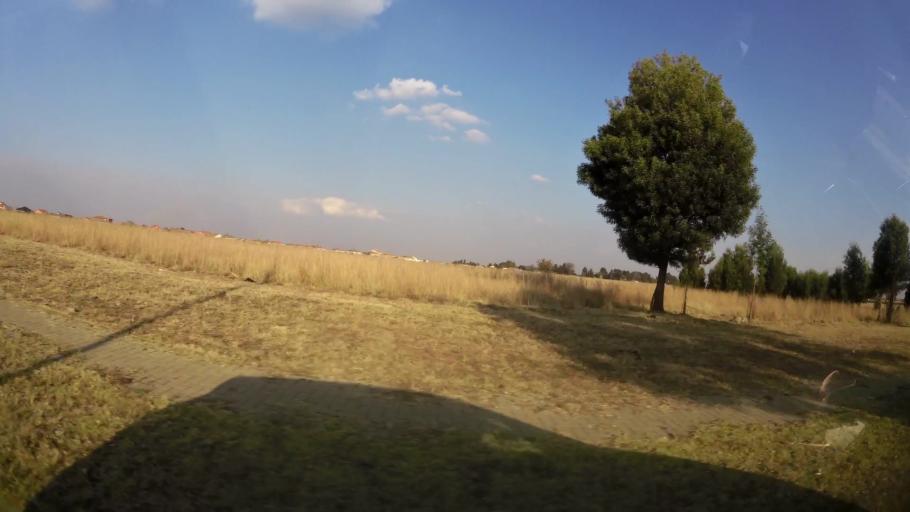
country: ZA
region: Gauteng
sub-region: Ekurhuleni Metropolitan Municipality
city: Benoni
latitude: -26.1372
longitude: 28.3758
